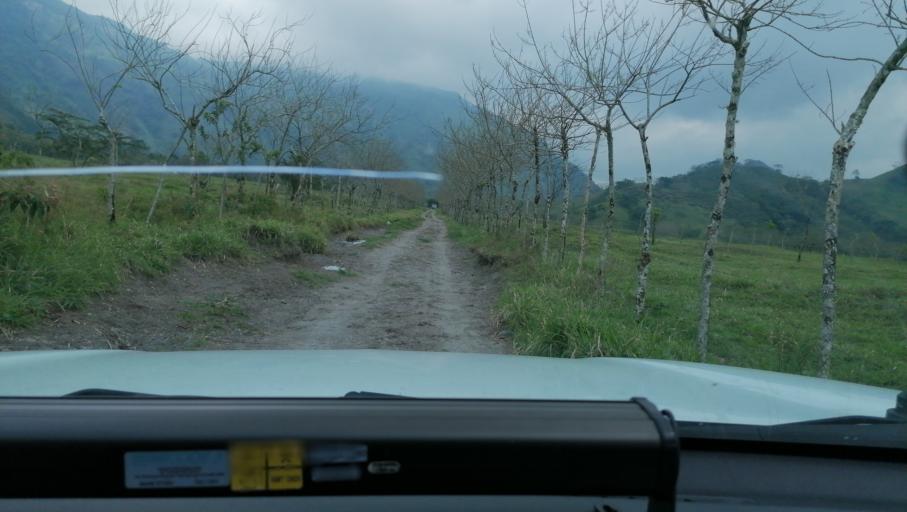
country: MX
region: Chiapas
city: Ixtacomitan
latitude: 17.3657
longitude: -93.1870
